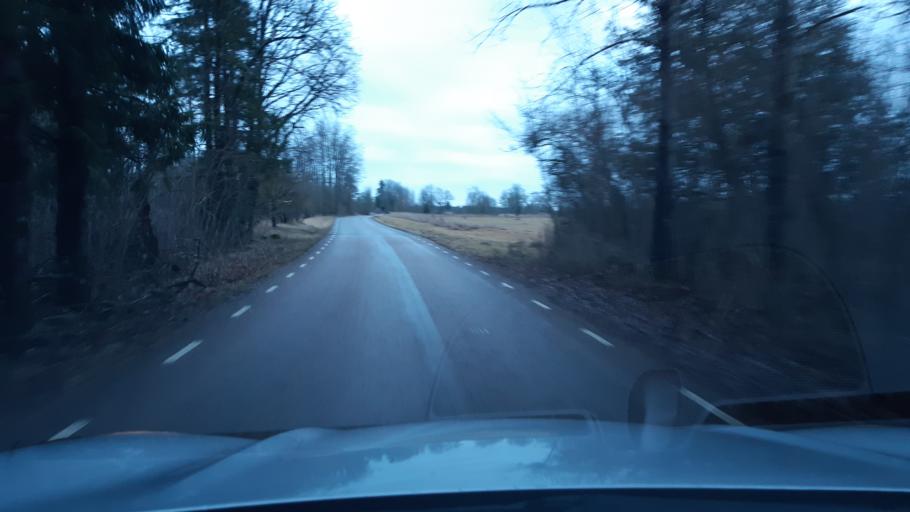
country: EE
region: Raplamaa
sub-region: Rapla vald
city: Rapla
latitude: 58.9962
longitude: 24.7193
